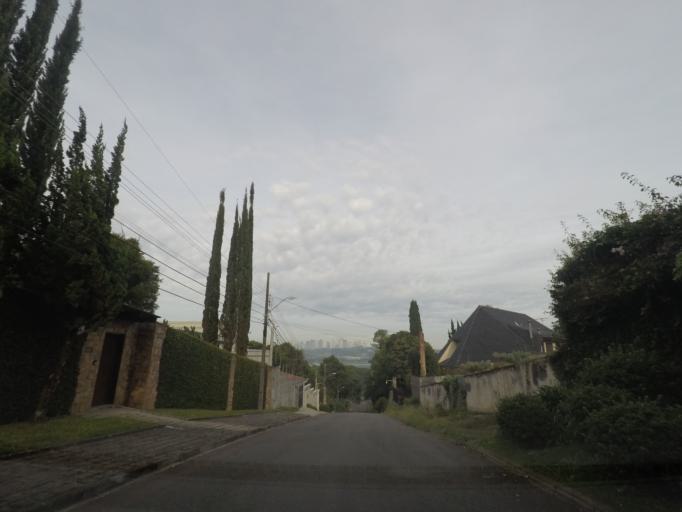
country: BR
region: Parana
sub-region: Curitiba
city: Curitiba
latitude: -25.4263
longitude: -49.3034
